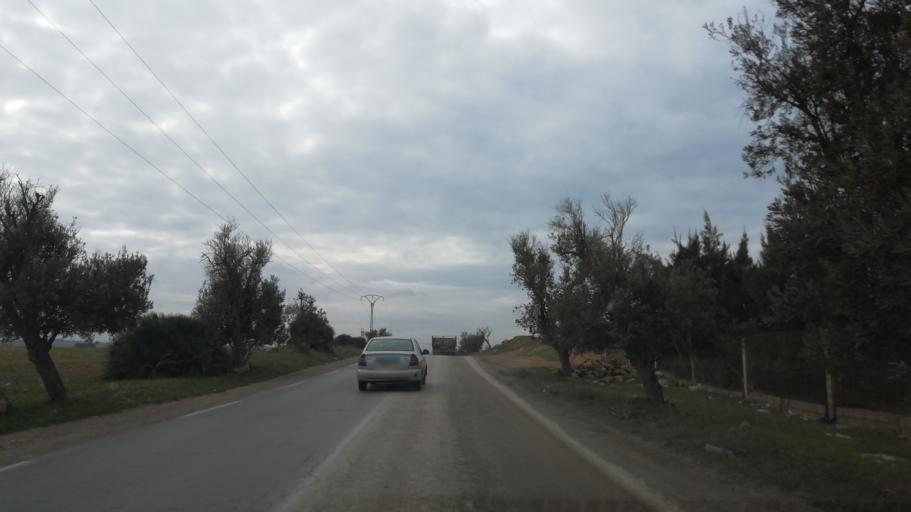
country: DZ
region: Oran
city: Ain el Bya
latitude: 35.7798
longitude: -0.3450
